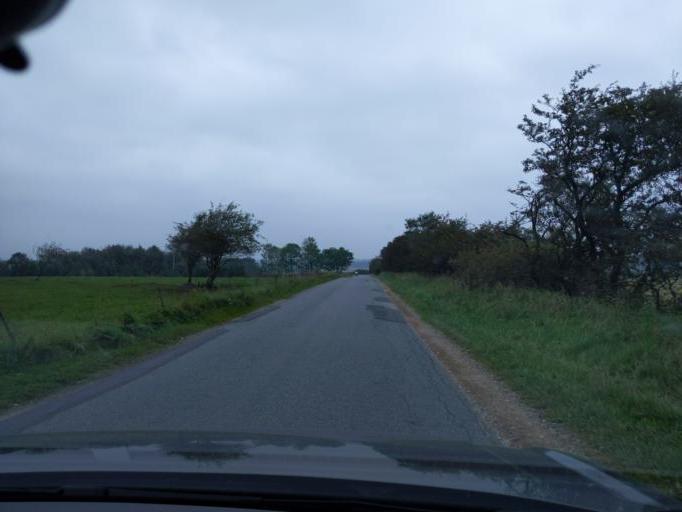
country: DK
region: Central Jutland
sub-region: Viborg Kommune
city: Stoholm
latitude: 56.4917
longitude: 9.2439
